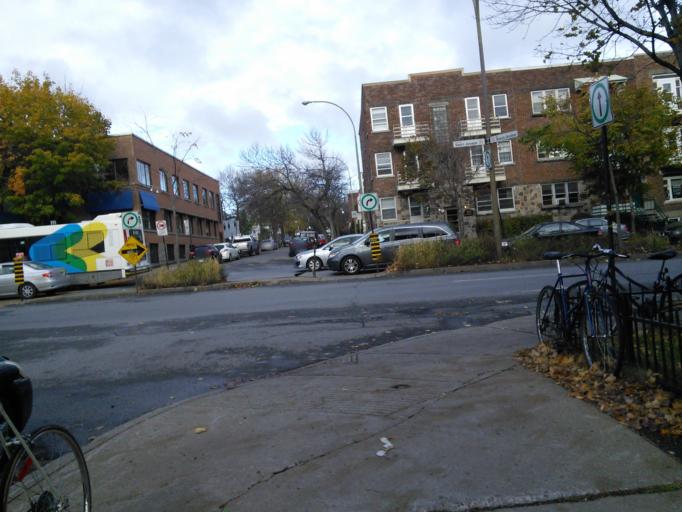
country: CA
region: Quebec
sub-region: Montreal
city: Montreal
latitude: 45.5286
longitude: -73.5853
